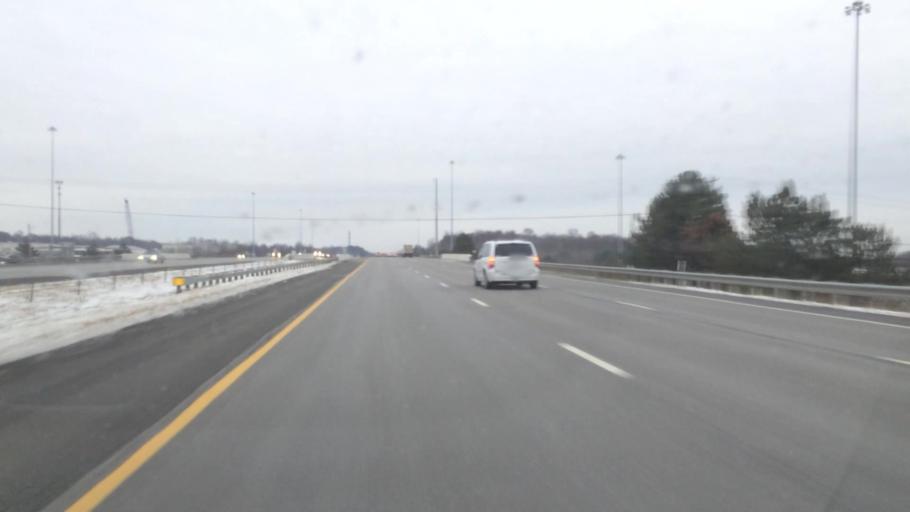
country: US
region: Ohio
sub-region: Medina County
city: Brunswick
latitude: 41.2397
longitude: -81.7989
